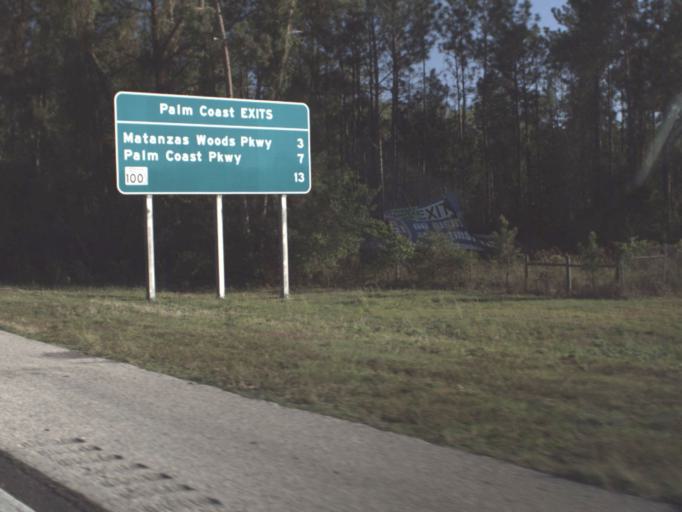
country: US
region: Florida
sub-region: Flagler County
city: Palm Coast
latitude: 29.6426
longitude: -81.2716
